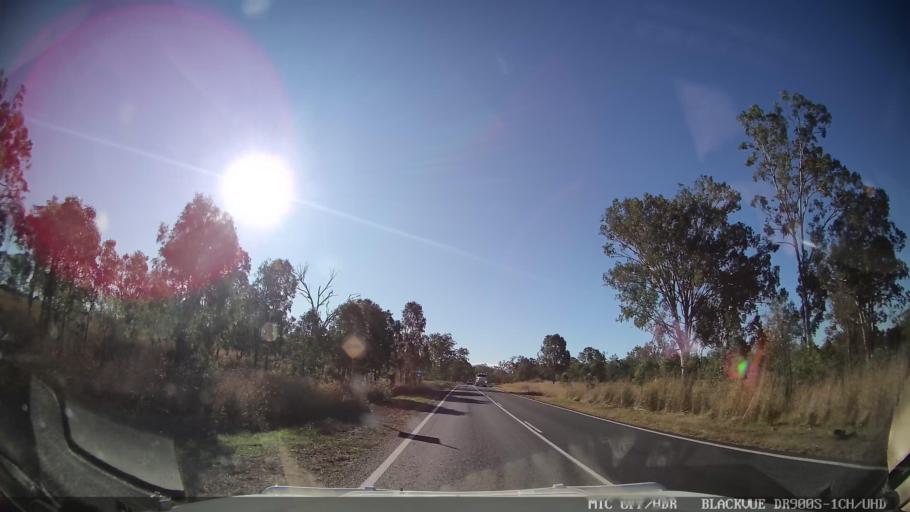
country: AU
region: Queensland
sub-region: Bundaberg
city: Sharon
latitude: -24.8251
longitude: 151.7066
